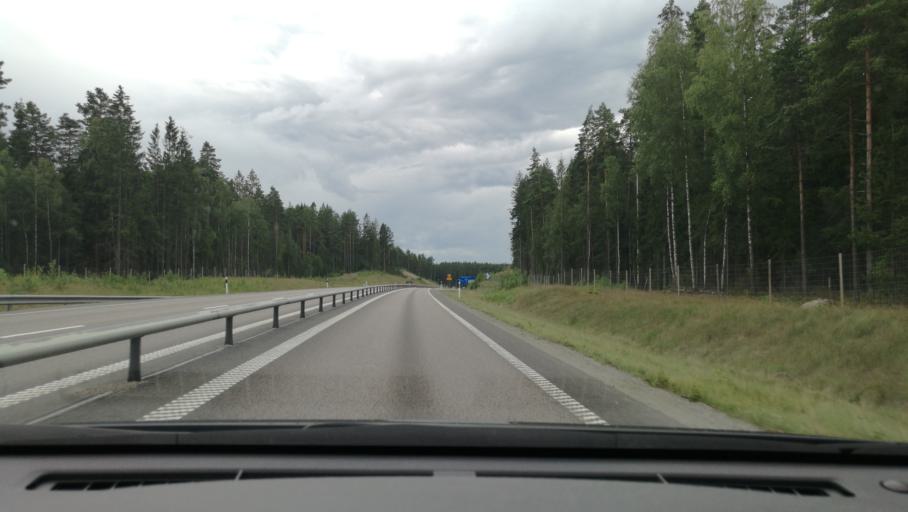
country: SE
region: Soedermanland
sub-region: Katrineholms Kommun
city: Katrineholm
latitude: 58.9768
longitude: 16.2651
